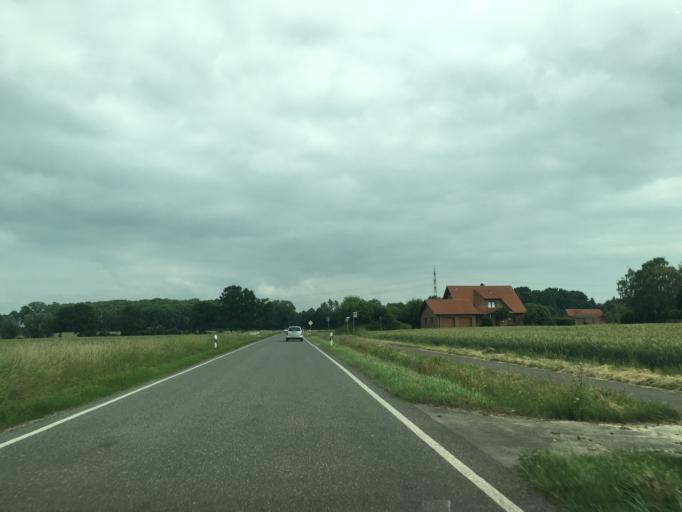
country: DE
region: North Rhine-Westphalia
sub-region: Regierungsbezirk Munster
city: Horstmar
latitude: 52.1054
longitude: 7.3129
